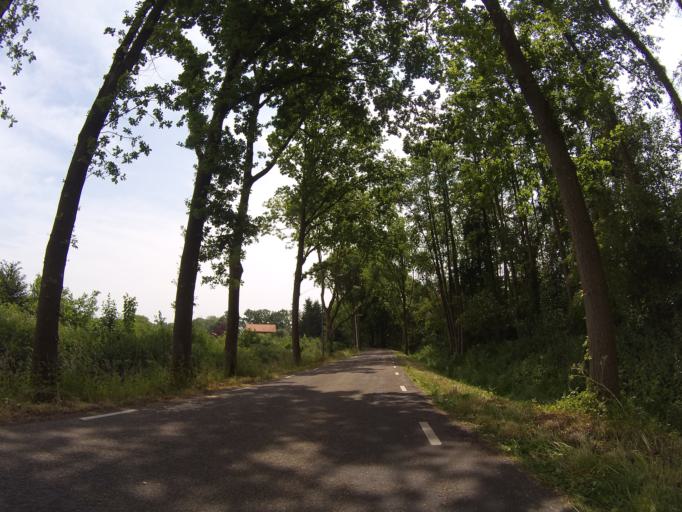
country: NL
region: Utrecht
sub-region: Gemeente Zeist
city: Zeist
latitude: 52.0723
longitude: 5.2288
